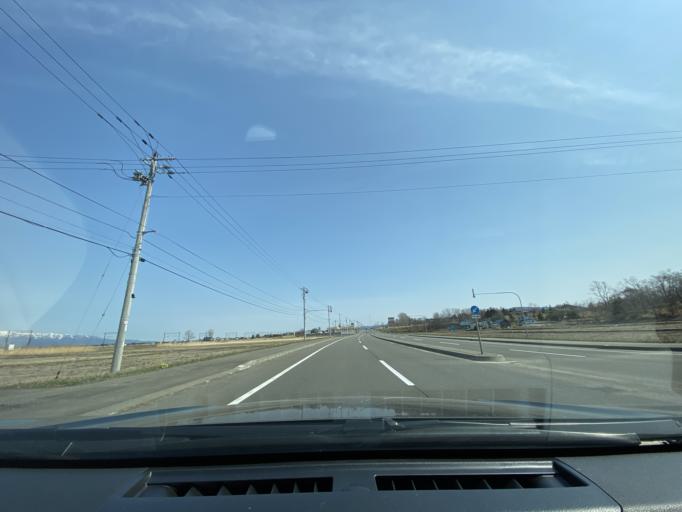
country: JP
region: Hokkaido
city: Iwamizawa
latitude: 43.2543
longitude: 141.8060
